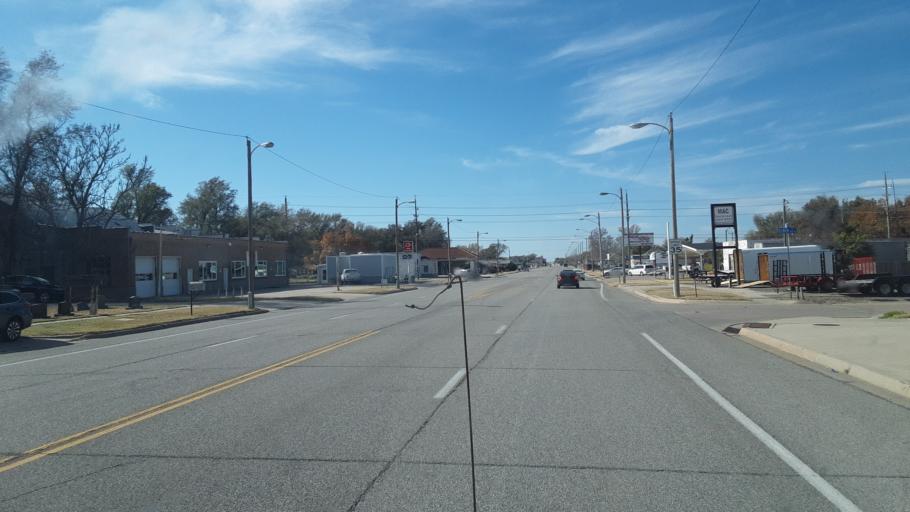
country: US
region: Kansas
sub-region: McPherson County
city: McPherson
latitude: 38.3693
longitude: -97.6749
